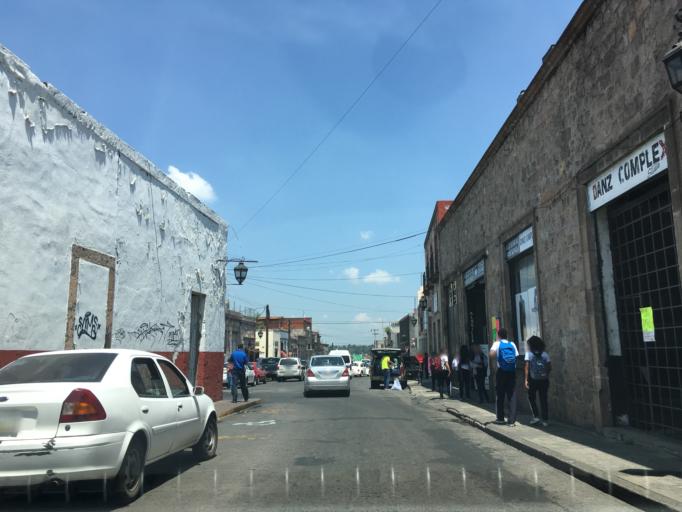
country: MX
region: Michoacan
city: Morelia
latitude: 19.7066
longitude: -101.1891
